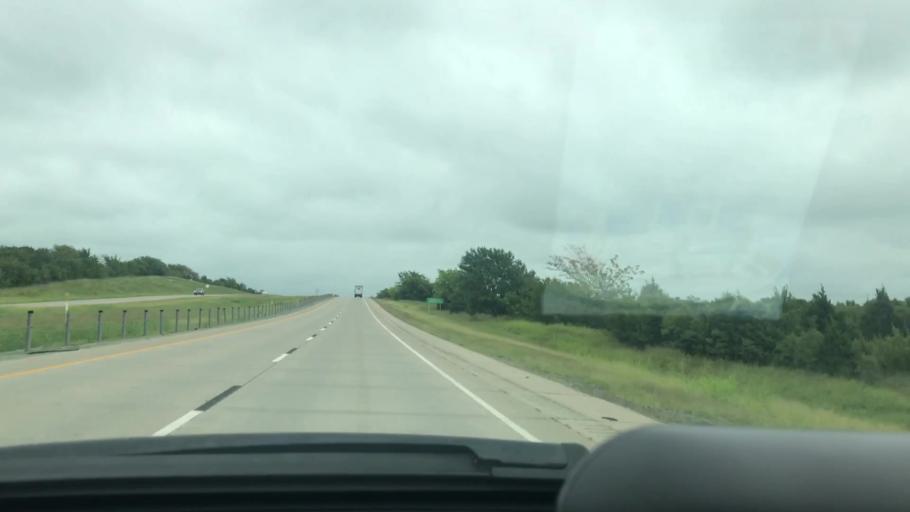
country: US
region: Oklahoma
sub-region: Pittsburg County
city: McAlester
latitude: 34.6811
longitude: -95.9288
